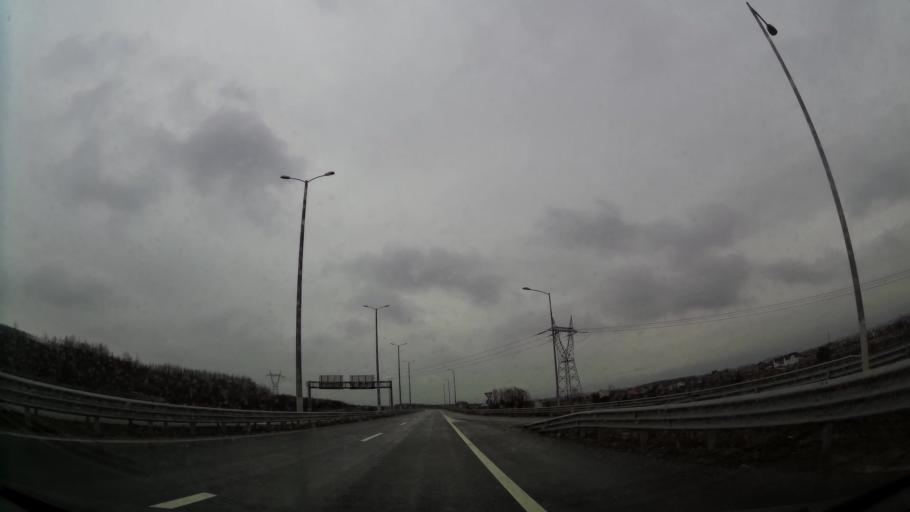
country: XK
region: Ferizaj
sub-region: Komuna e Ferizajt
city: Ferizaj
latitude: 42.3671
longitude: 21.2045
